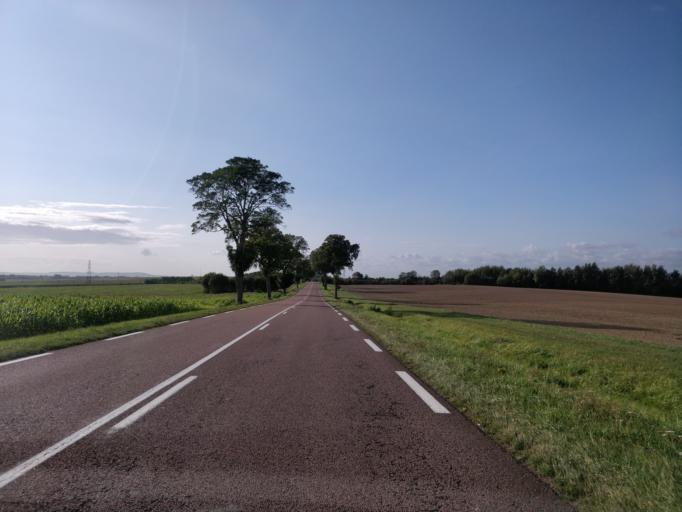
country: FR
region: Champagne-Ardenne
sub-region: Departement de l'Aube
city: Verrieres
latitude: 48.2831
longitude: 4.1740
